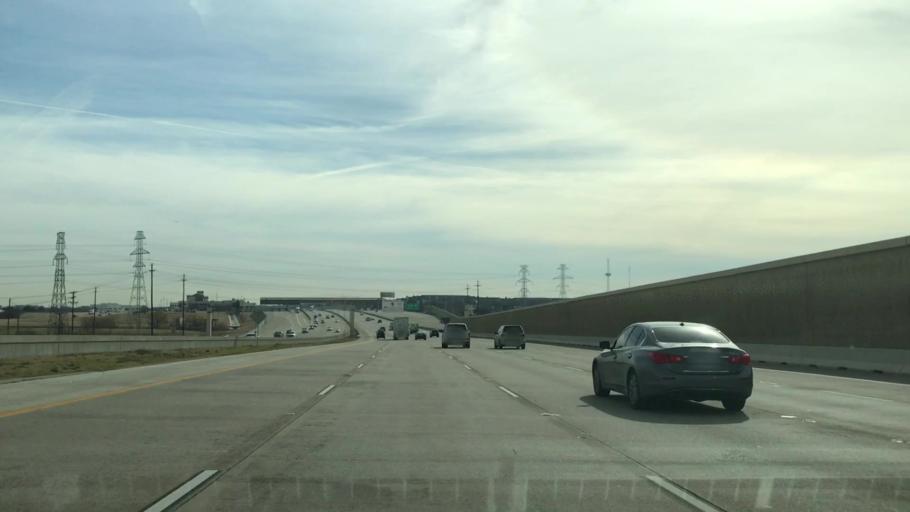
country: US
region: Texas
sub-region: Dallas County
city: Addison
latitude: 33.0067
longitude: -96.7827
